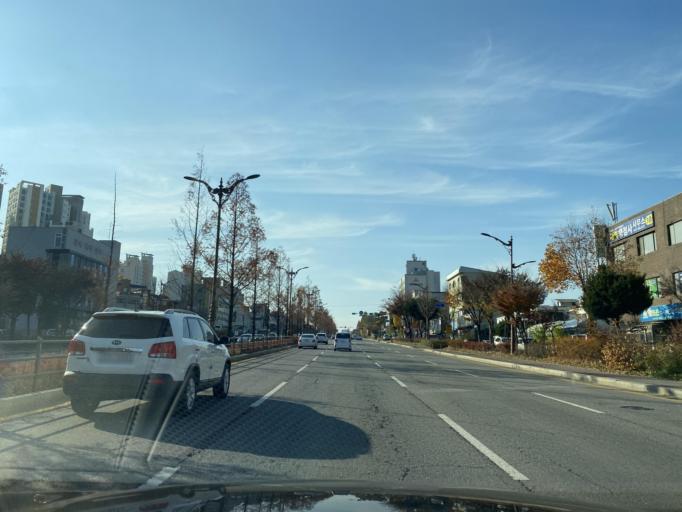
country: KR
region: Chungcheongnam-do
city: Cheonan
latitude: 36.7986
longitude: 127.1418
